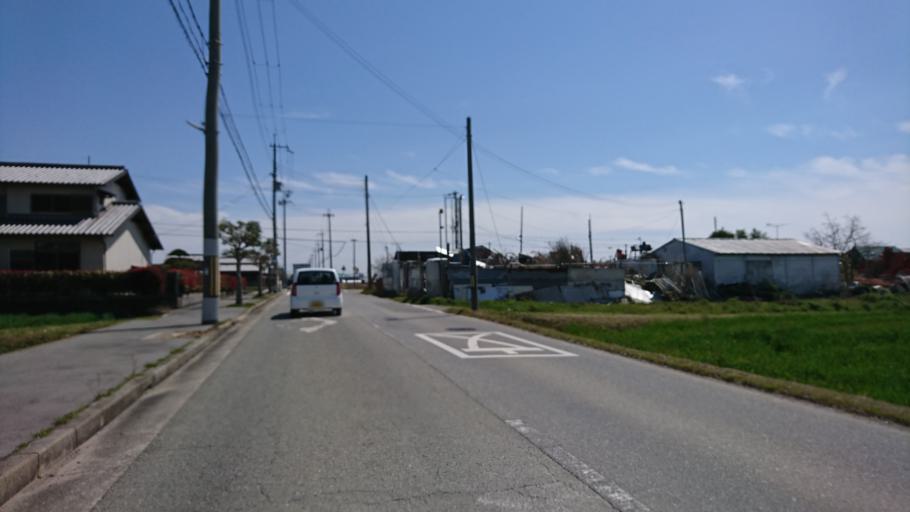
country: JP
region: Hyogo
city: Kakogawacho-honmachi
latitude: 34.7395
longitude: 134.8947
